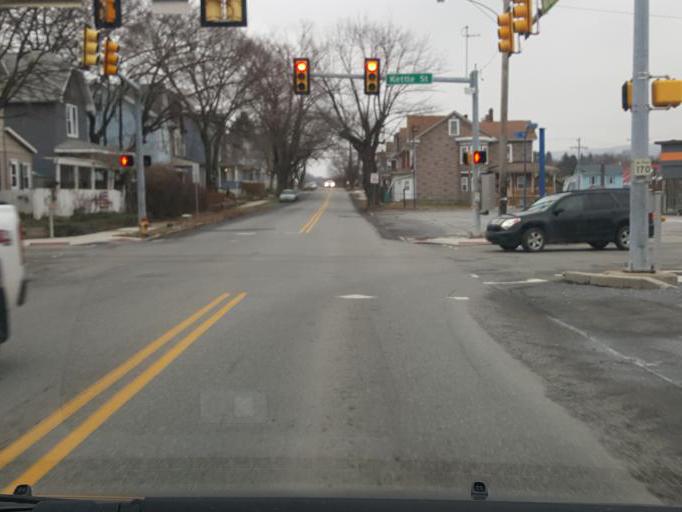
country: US
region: Pennsylvania
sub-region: Blair County
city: Altoona
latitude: 40.5207
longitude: -78.3781
